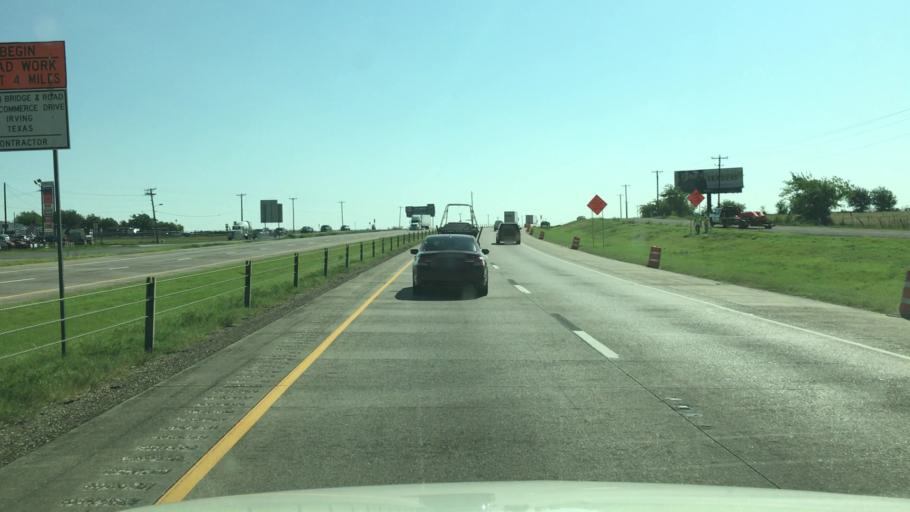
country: US
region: Texas
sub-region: Rockwall County
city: Royse City
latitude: 32.9797
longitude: -96.3049
